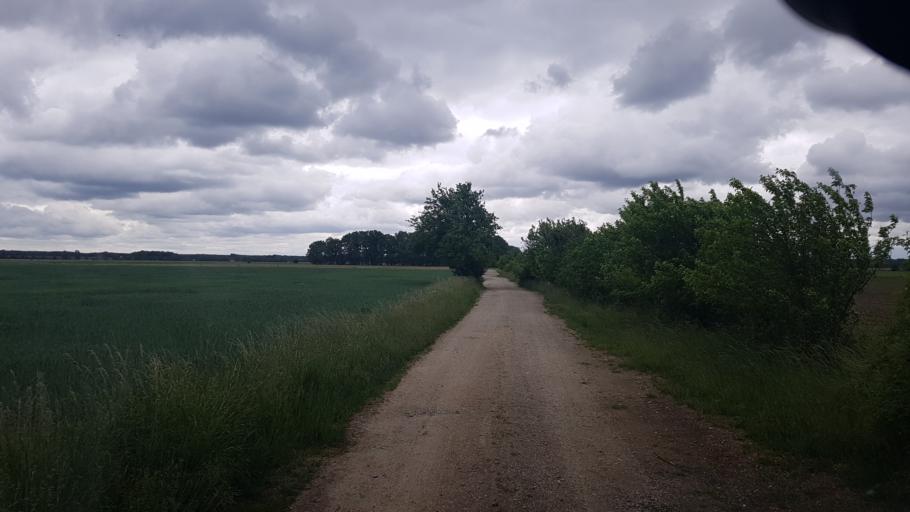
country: DE
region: Brandenburg
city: Ruckersdorf
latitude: 51.5835
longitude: 13.5431
